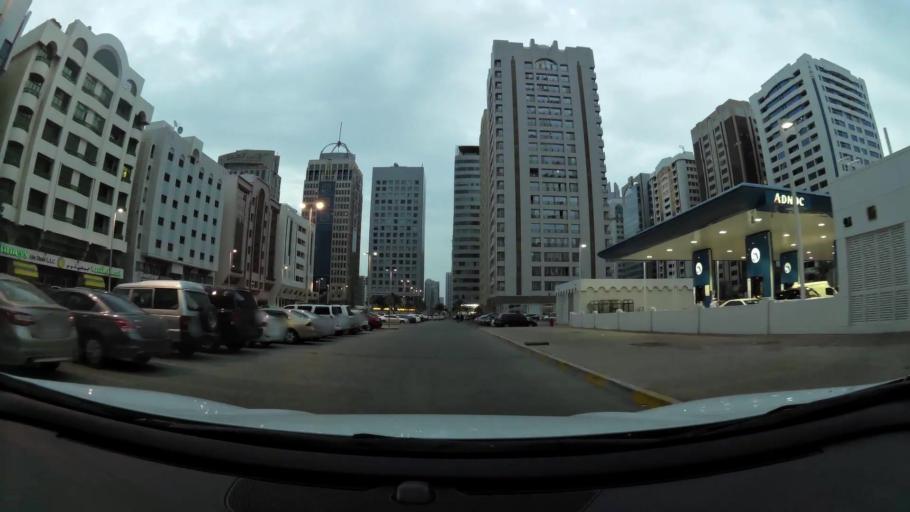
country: AE
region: Abu Dhabi
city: Abu Dhabi
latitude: 24.4898
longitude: 54.3712
